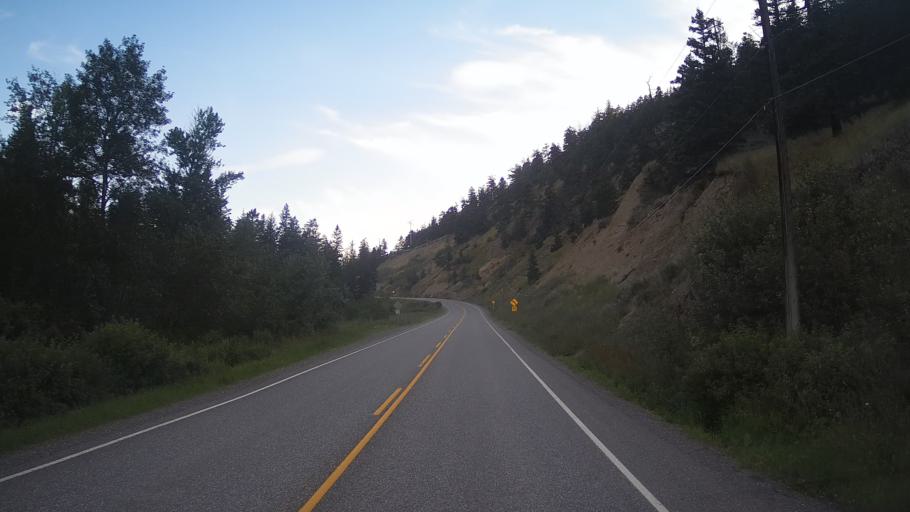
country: CA
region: British Columbia
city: Cache Creek
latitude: 50.8678
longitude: -121.5247
